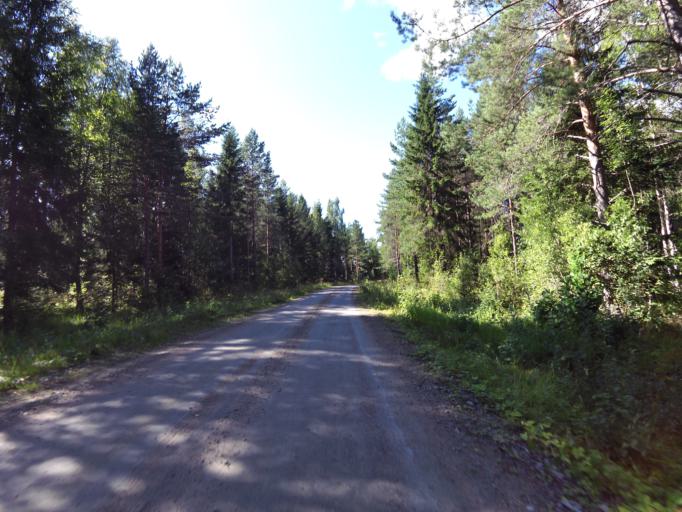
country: SE
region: Gaevleborg
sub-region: Ockelbo Kommun
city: Ockelbo
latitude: 60.7945
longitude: 16.8227
